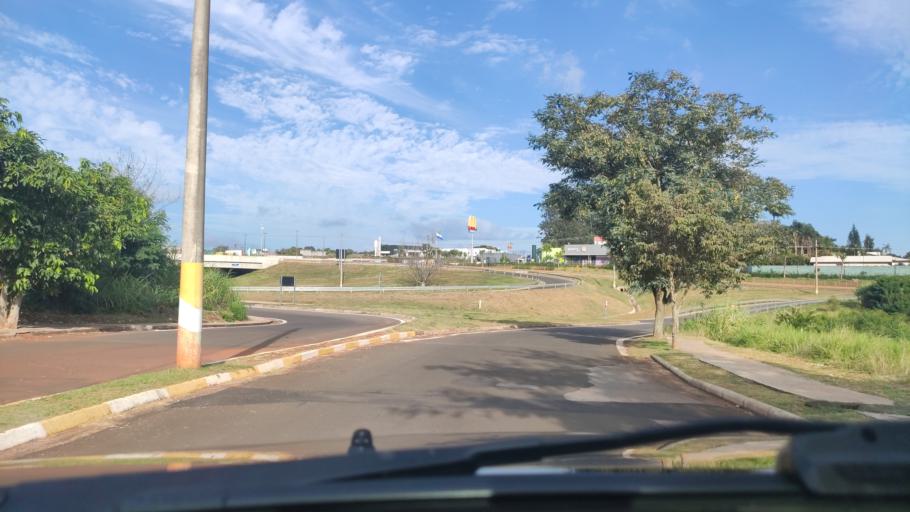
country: BR
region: Sao Paulo
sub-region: Avare
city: Avare
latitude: -23.0950
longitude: -48.9372
